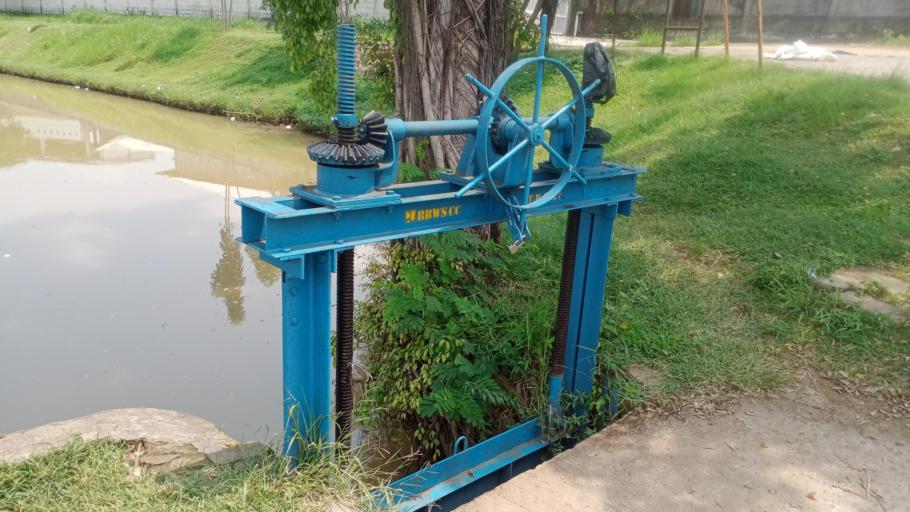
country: ID
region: West Java
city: Cileungsir
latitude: -6.3500
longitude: 107.0383
